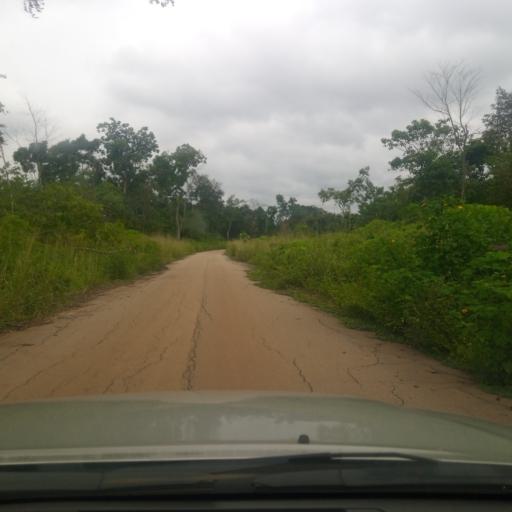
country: NG
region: Ebonyi
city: Effium
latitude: 6.6257
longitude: 8.0493
